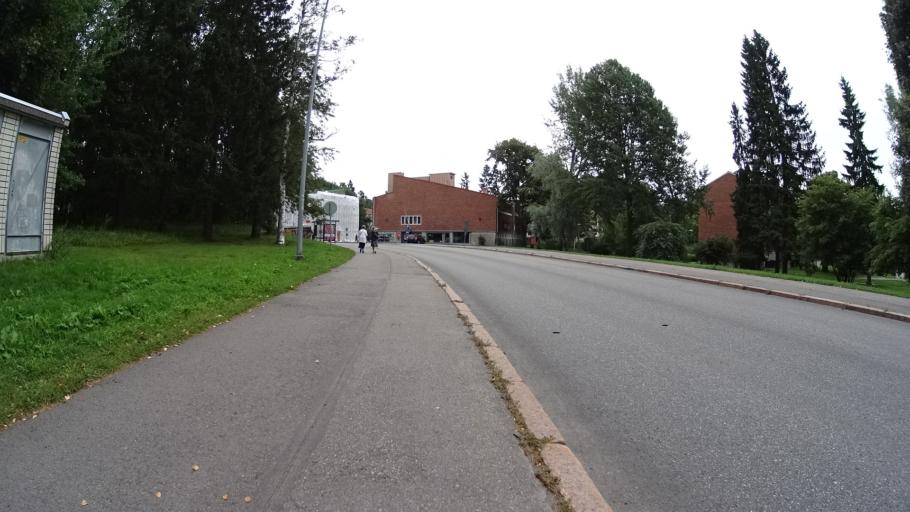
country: FI
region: Uusimaa
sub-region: Helsinki
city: Helsinki
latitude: 60.2282
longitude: 24.9249
